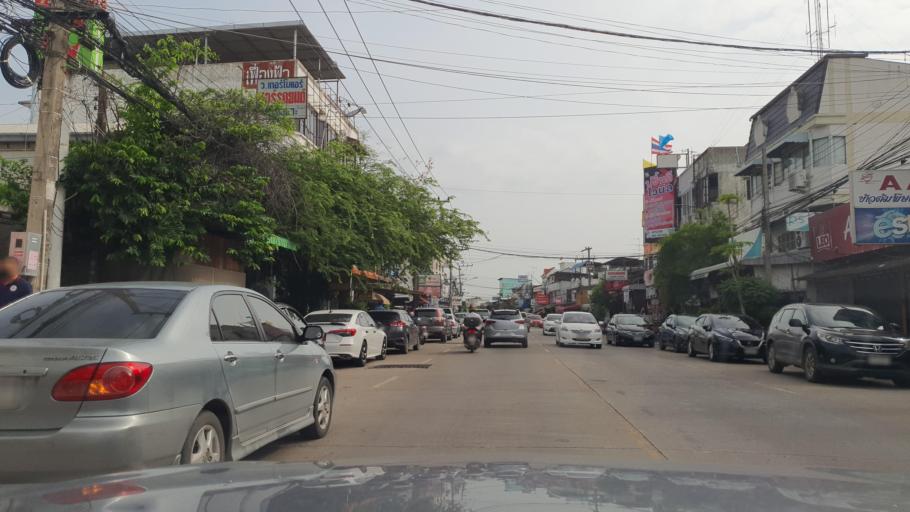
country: TH
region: Phitsanulok
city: Phitsanulok
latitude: 16.8272
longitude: 100.2653
